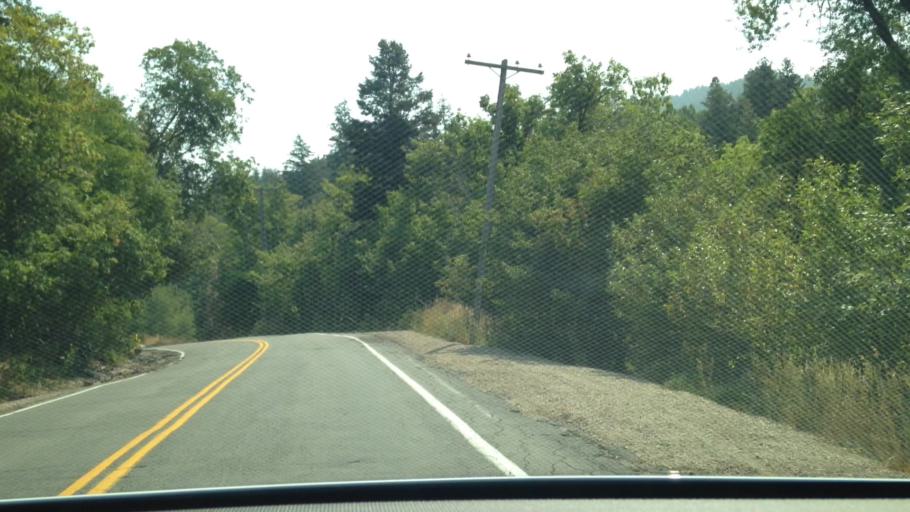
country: US
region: Utah
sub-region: Salt Lake County
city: Mount Olympus
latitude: 40.6994
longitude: -111.7211
